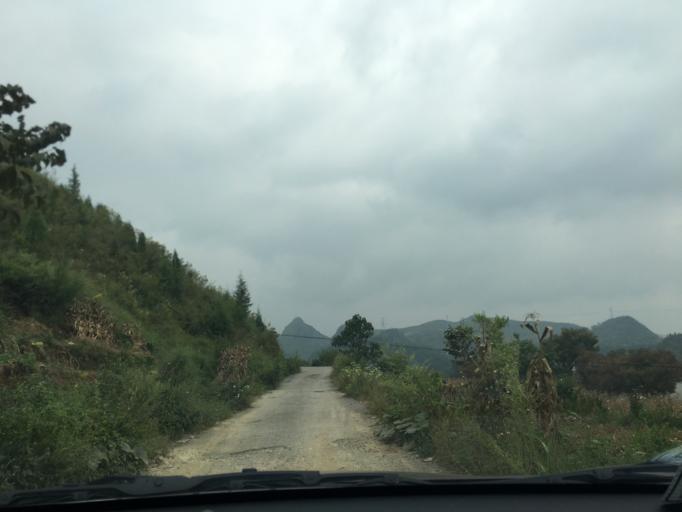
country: CN
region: Guizhou Sheng
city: Anshun
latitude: 25.5731
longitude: 105.6274
